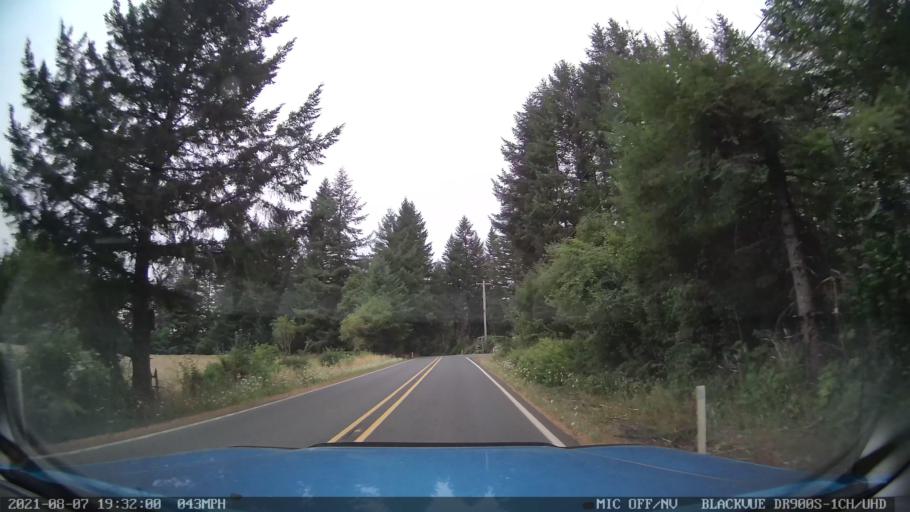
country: US
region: Oregon
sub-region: Linn County
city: Lyons
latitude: 44.8964
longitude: -122.6389
